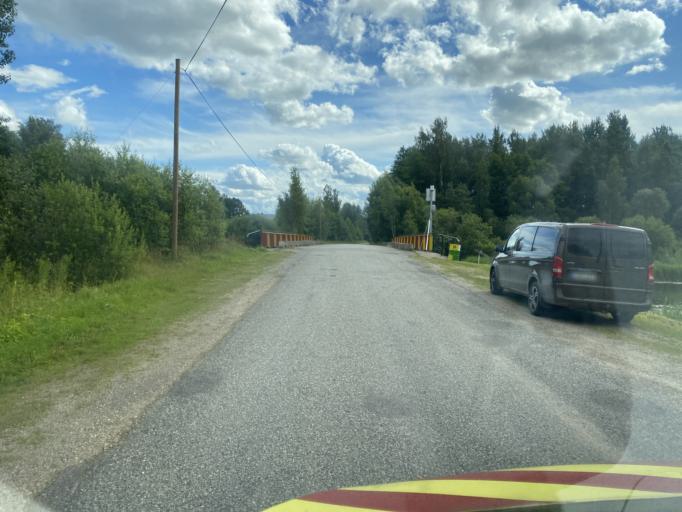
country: EE
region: Viljandimaa
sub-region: Viiratsi vald
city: Viiratsi
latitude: 58.3953
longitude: 25.8223
